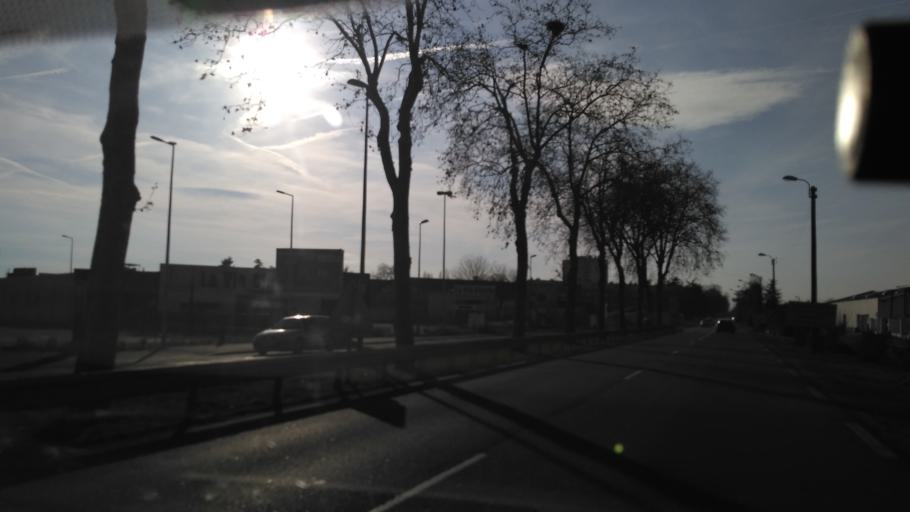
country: FR
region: Rhone-Alpes
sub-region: Departement de la Drome
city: Bourg-de-Peage
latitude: 45.0515
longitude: 5.0820
